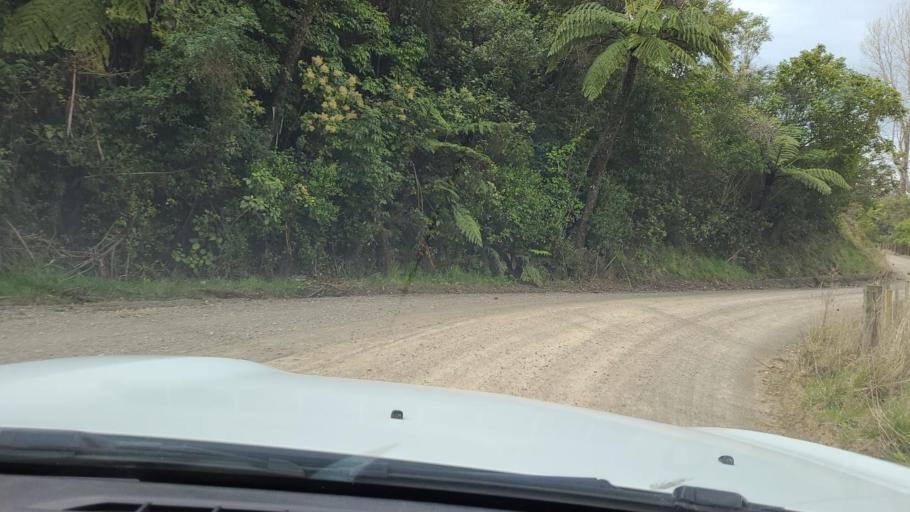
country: NZ
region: Hawke's Bay
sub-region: Napier City
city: Napier
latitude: -39.2809
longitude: 176.8386
